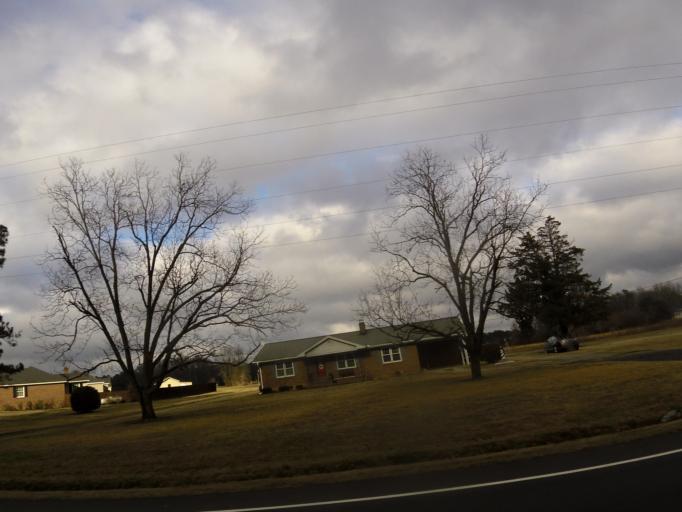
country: US
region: North Carolina
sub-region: Nash County
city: Rocky Mount
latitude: 35.9094
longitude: -77.7466
